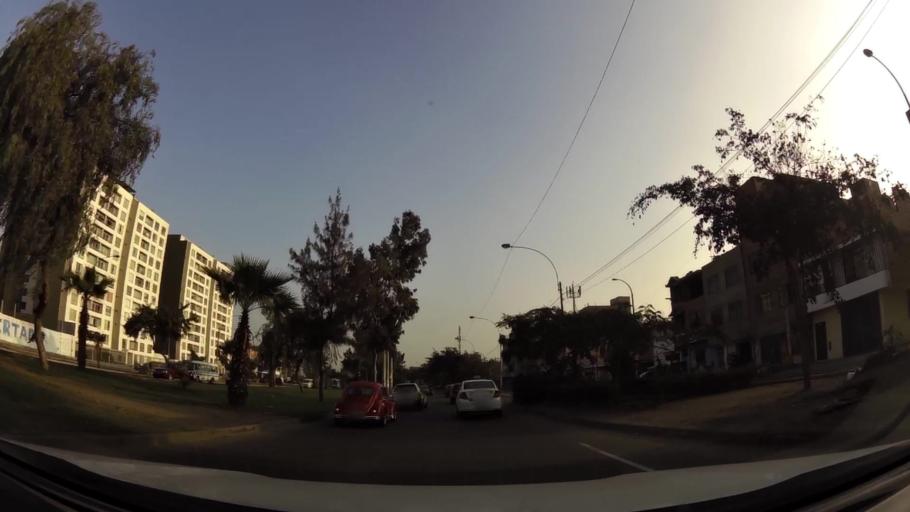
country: PE
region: Lima
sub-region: Lima
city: Independencia
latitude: -11.9660
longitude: -77.0742
